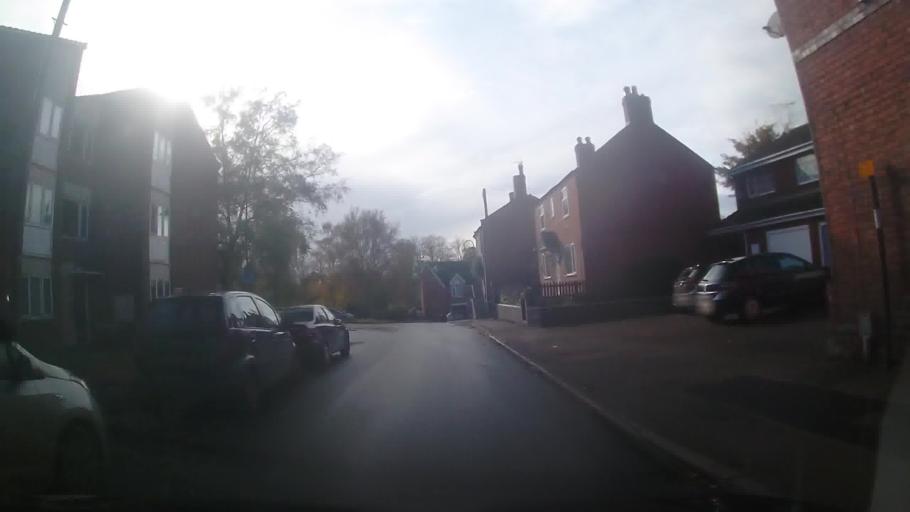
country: GB
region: England
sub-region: Shropshire
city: Whitchurch
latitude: 52.9703
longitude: -2.6867
